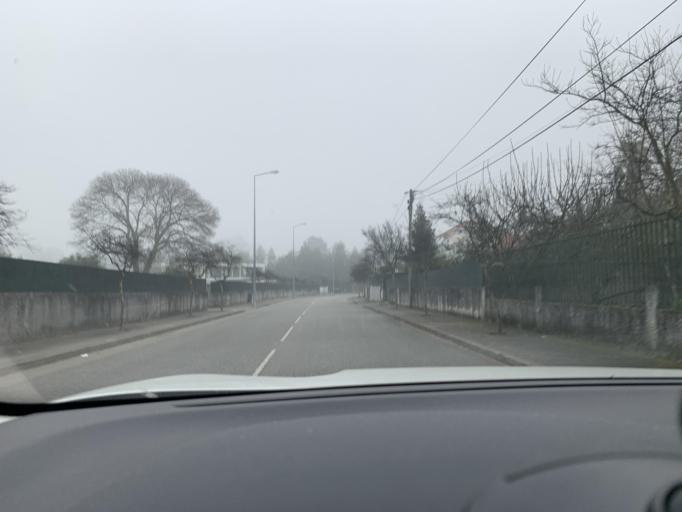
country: PT
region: Viseu
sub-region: Viseu
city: Viseu
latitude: 40.6373
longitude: -7.9192
